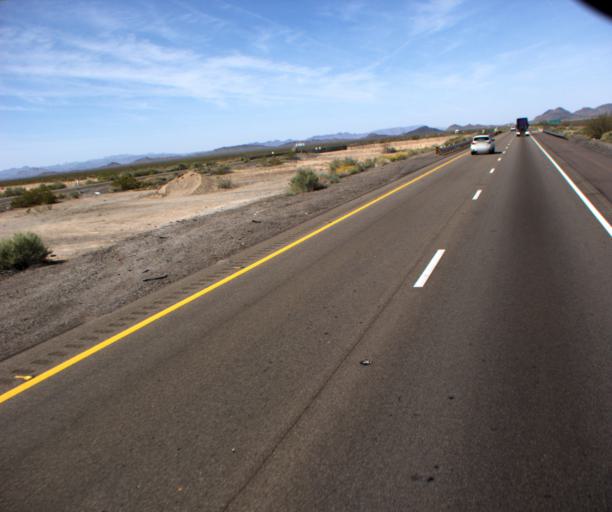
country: US
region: Arizona
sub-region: La Paz County
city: Salome
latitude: 33.5958
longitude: -113.5291
